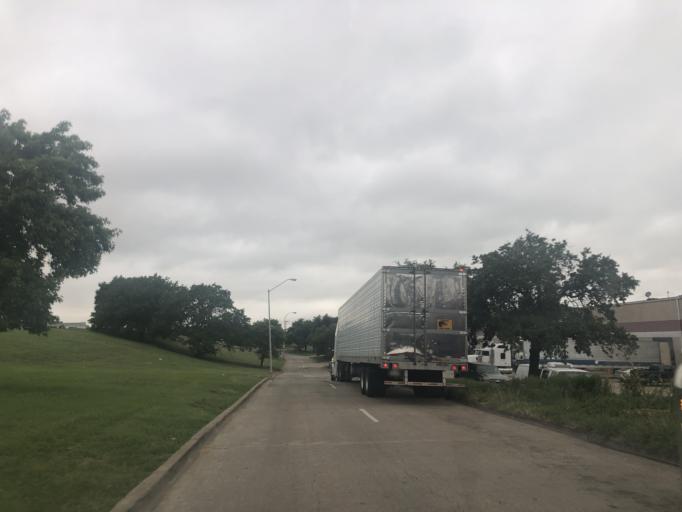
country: US
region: Texas
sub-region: Dallas County
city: Cockrell Hill
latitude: 32.7735
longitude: -96.8632
